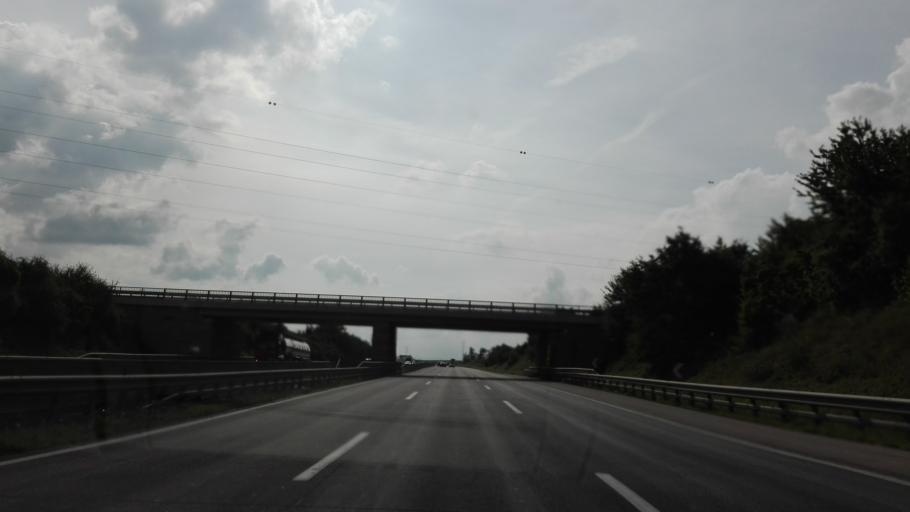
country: AT
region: Lower Austria
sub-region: Politischer Bezirk Melk
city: Loosdorf
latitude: 48.1926
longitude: 15.3876
